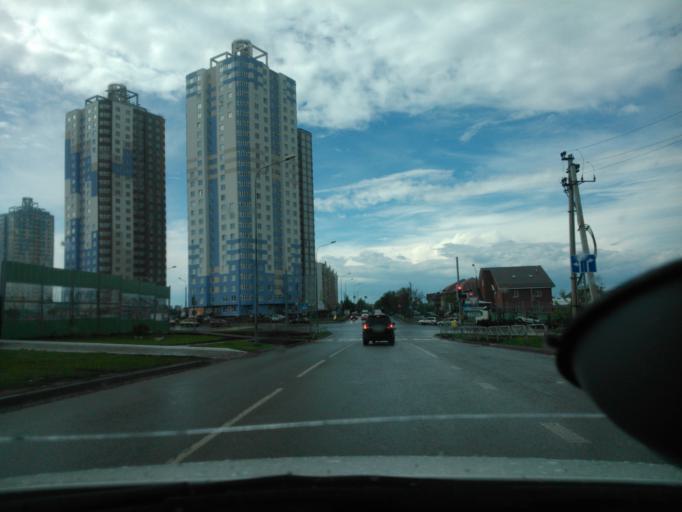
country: RU
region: Perm
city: Perm
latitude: 58.0042
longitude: 56.3285
